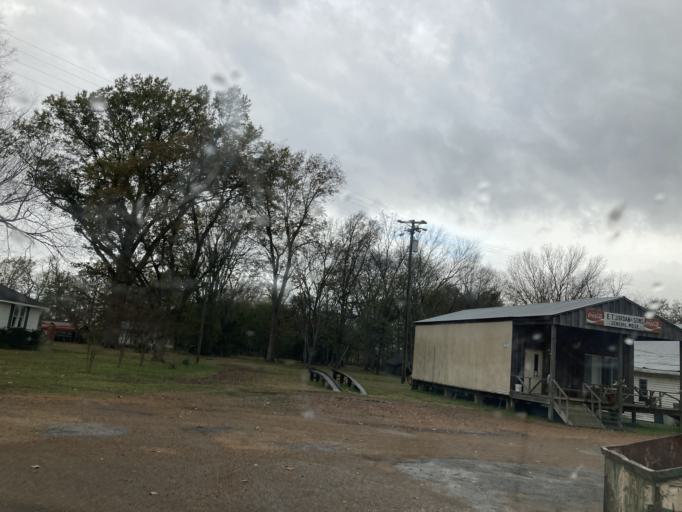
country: US
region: Mississippi
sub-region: Yazoo County
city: Yazoo City
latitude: 32.9888
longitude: -90.4479
